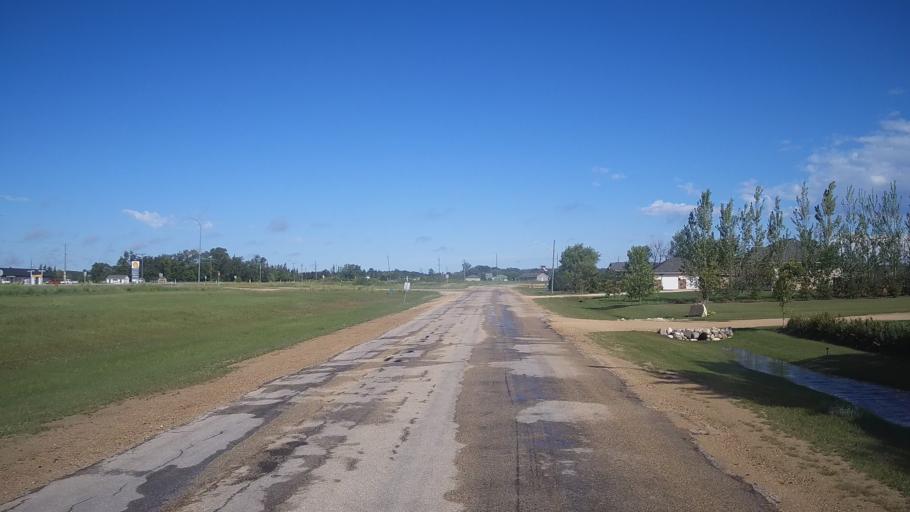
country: CA
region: Manitoba
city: Stonewall
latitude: 50.2089
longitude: -97.6636
